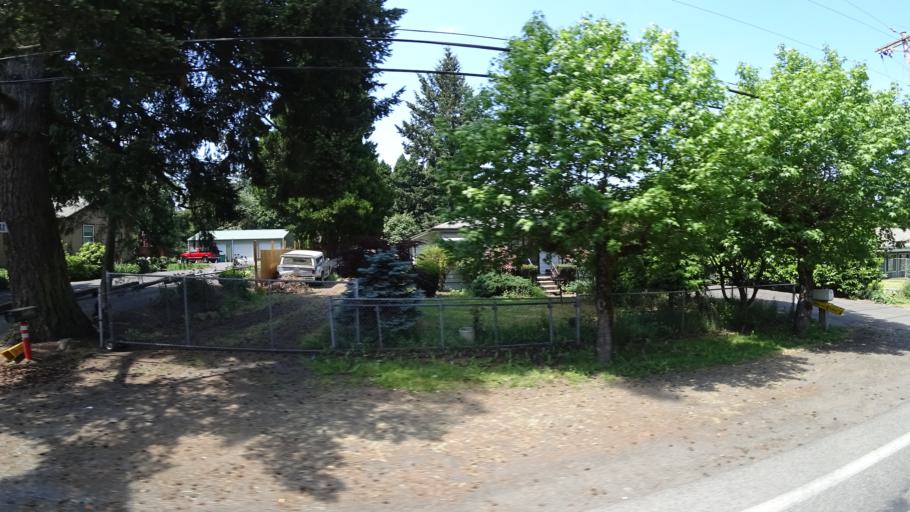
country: US
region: Oregon
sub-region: Clackamas County
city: Happy Valley
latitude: 45.4782
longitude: -122.5236
